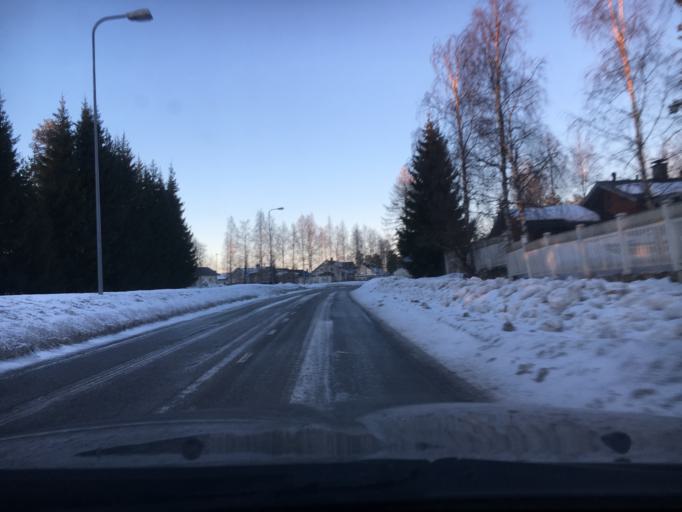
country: FI
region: Kainuu
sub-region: Kajaani
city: Kajaani
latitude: 64.2295
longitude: 27.7768
